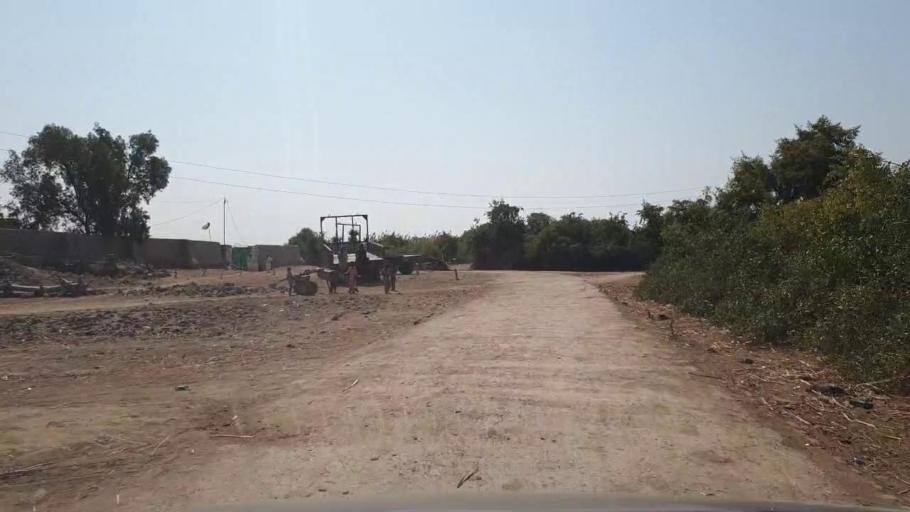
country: PK
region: Sindh
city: Samaro
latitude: 25.2316
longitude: 69.2537
